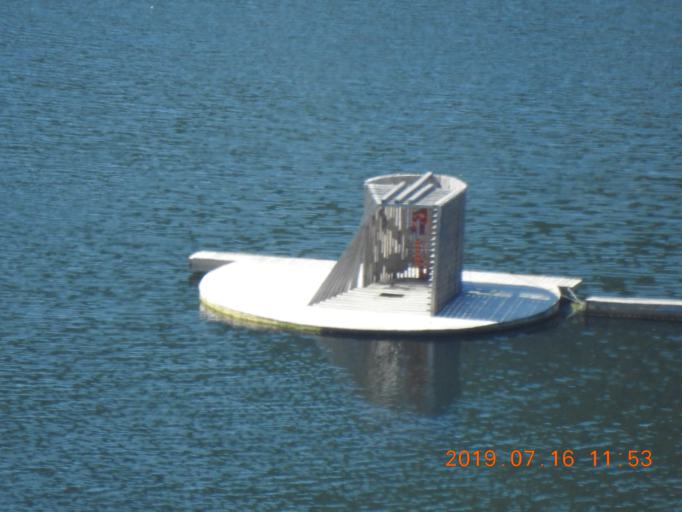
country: NO
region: Hordaland
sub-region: Bergen
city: Bergen
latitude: 60.3907
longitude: 5.3493
